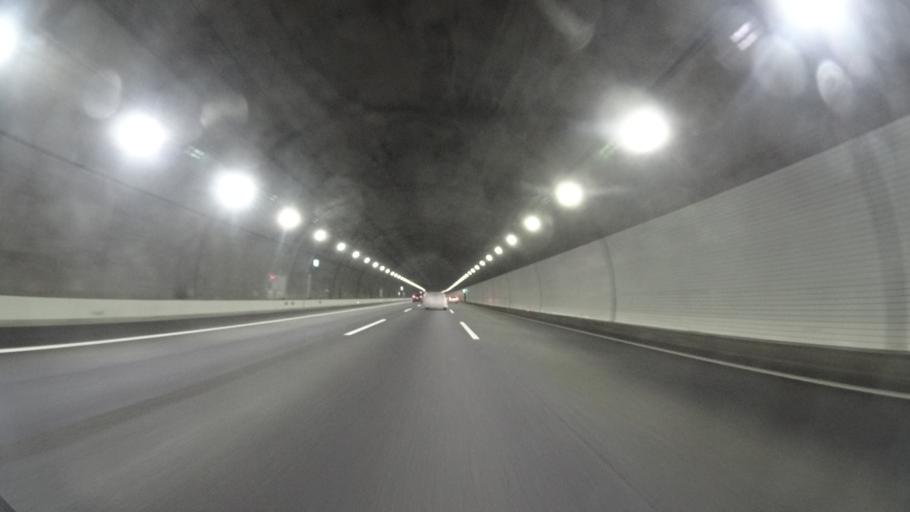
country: JP
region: Shizuoka
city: Fujinomiya
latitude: 35.1582
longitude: 138.5542
